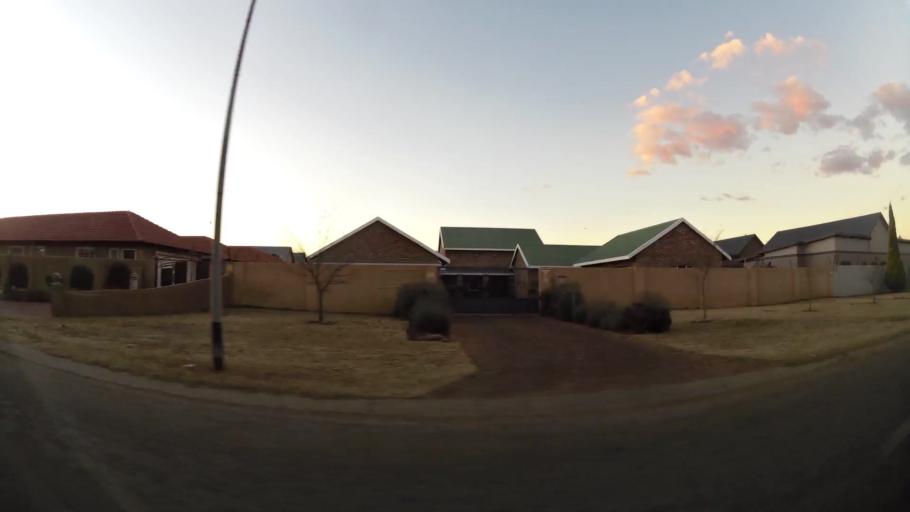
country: ZA
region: North-West
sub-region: Dr Kenneth Kaunda District Municipality
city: Potchefstroom
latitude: -26.7142
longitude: 27.1221
